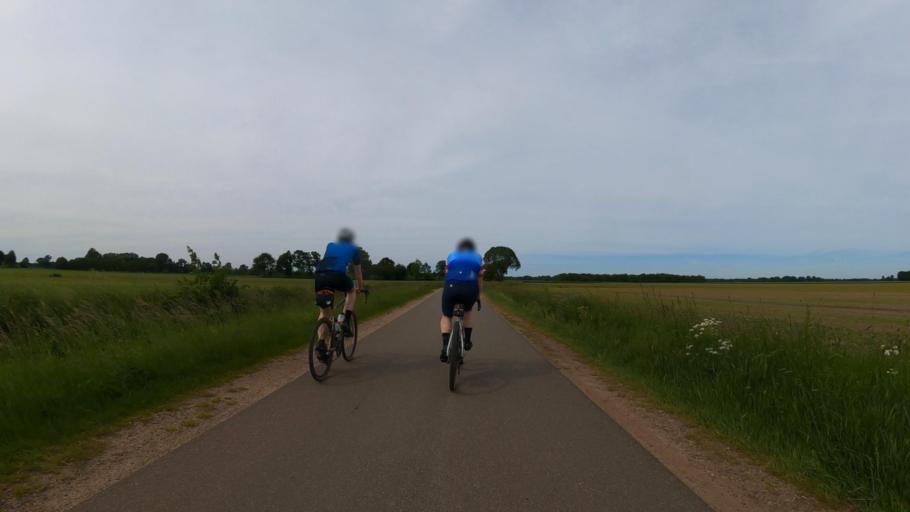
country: DE
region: Schleswig-Holstein
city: Sievershutten
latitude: 53.8700
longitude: 10.0853
